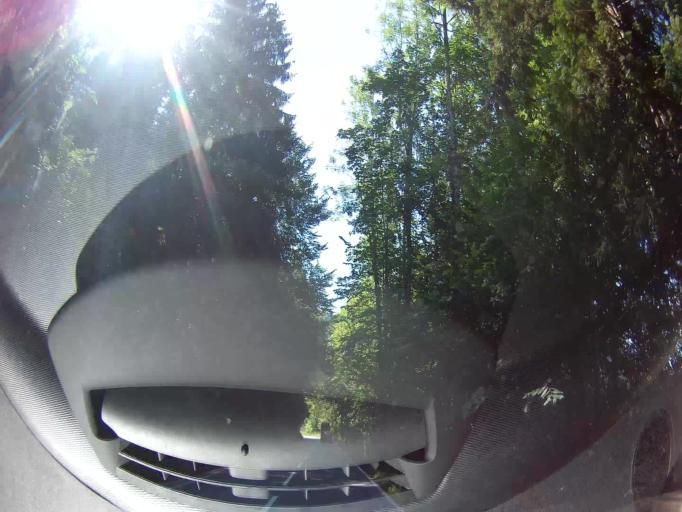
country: DE
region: Bavaria
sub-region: Upper Bavaria
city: Marktschellenberg
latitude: 47.6471
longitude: 13.0572
